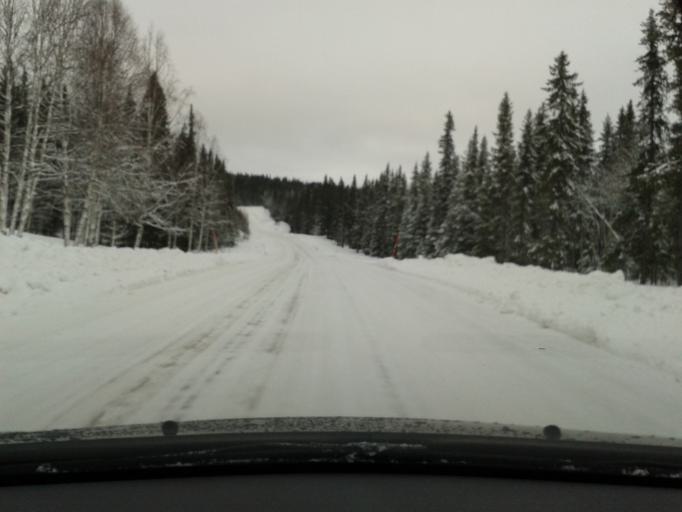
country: SE
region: Vaesterbotten
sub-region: Vilhelmina Kommun
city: Sjoberg
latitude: 65.2287
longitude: 15.9717
